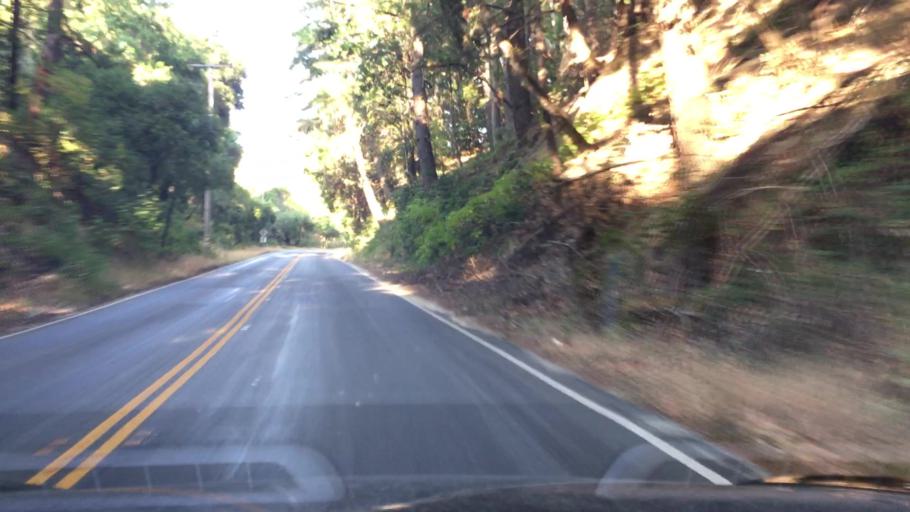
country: US
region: California
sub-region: Santa Clara County
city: Los Altos Hills
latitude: 37.3122
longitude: -122.1792
